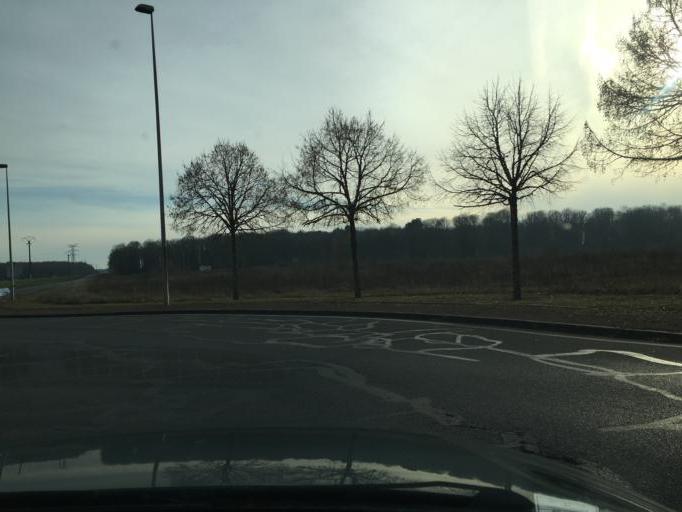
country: FR
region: Centre
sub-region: Departement du Loiret
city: Saint-Cyr-en-Val
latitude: 47.8209
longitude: 1.9703
